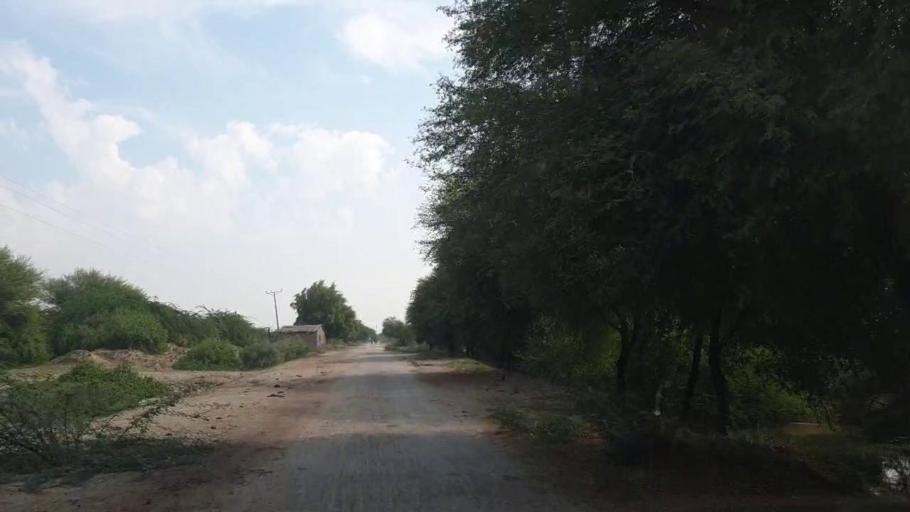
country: PK
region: Sindh
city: Tando Bago
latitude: 24.9247
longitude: 69.0185
